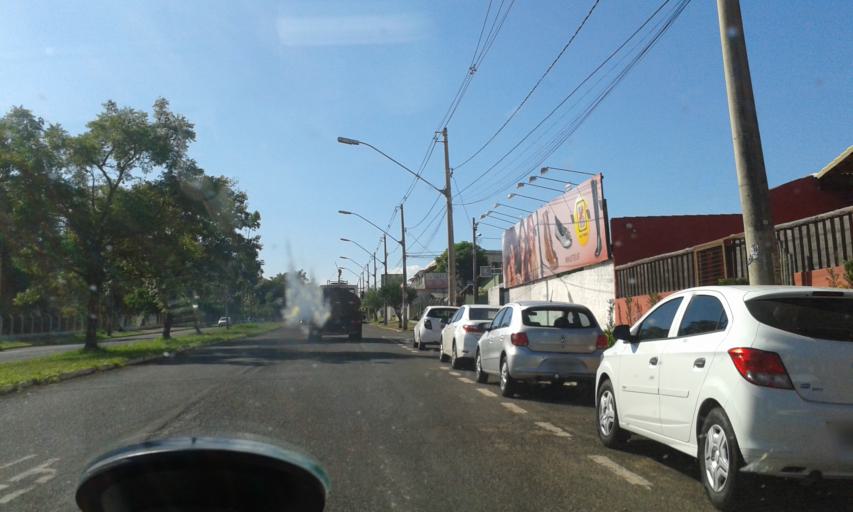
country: BR
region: Minas Gerais
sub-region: Uberlandia
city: Uberlandia
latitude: -18.9120
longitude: -48.2420
